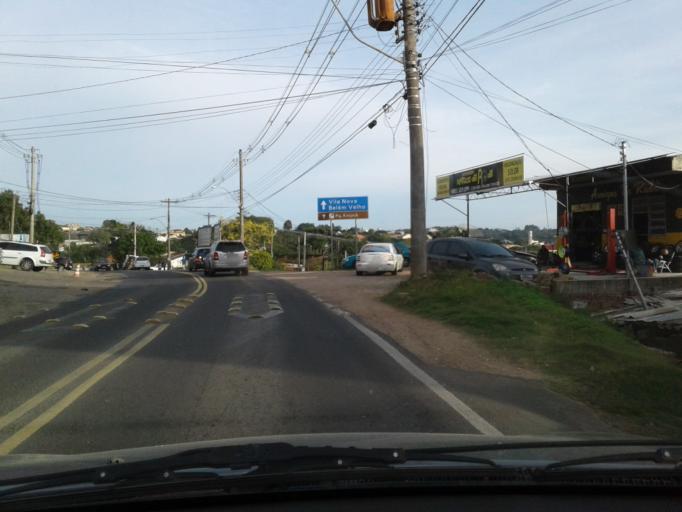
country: BR
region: Rio Grande do Sul
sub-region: Porto Alegre
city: Porto Alegre
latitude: -30.0995
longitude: -51.2254
